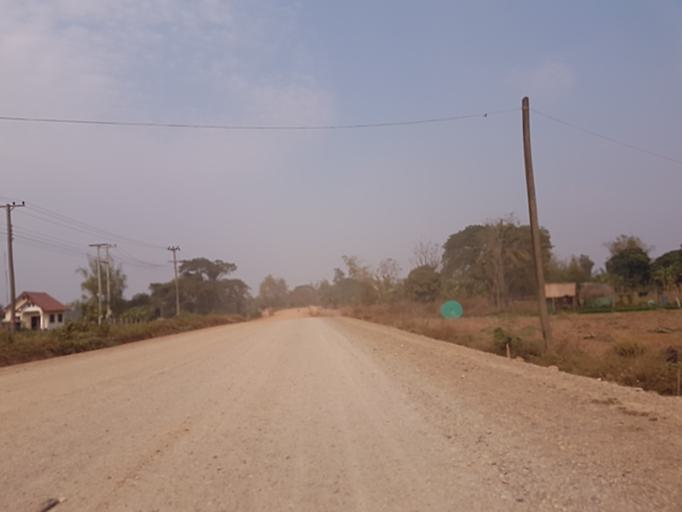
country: TH
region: Nong Khai
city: Nong Khai
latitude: 17.9728
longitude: 102.8499
